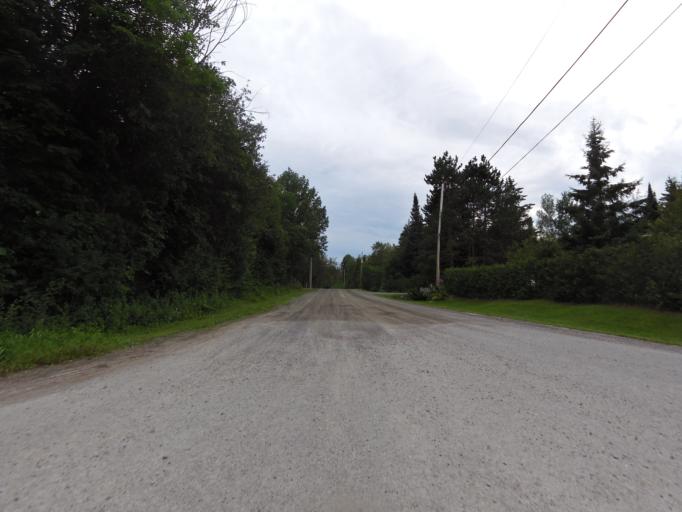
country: CA
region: Ontario
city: Carleton Place
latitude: 45.1520
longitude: -76.2120
